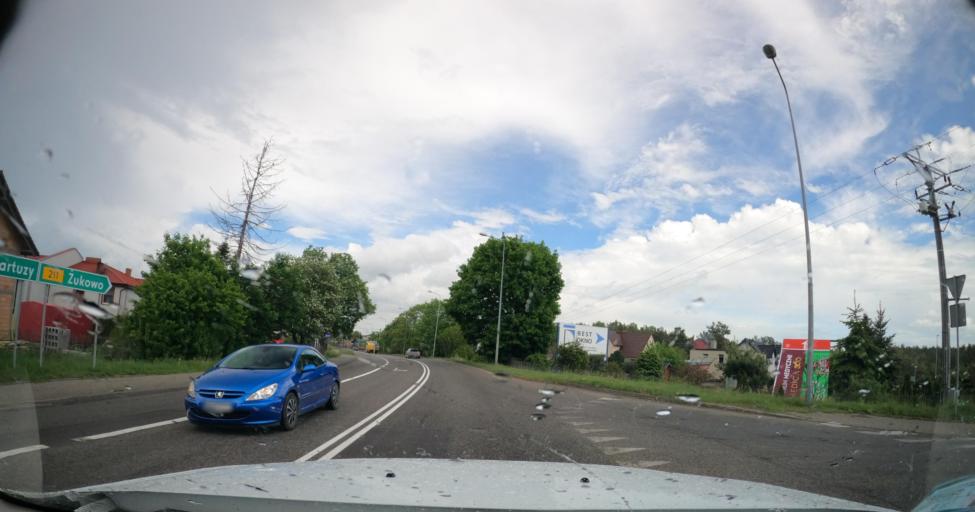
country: PL
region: Pomeranian Voivodeship
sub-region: Powiat kartuski
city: Przodkowo
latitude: 54.3154
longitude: 18.2822
